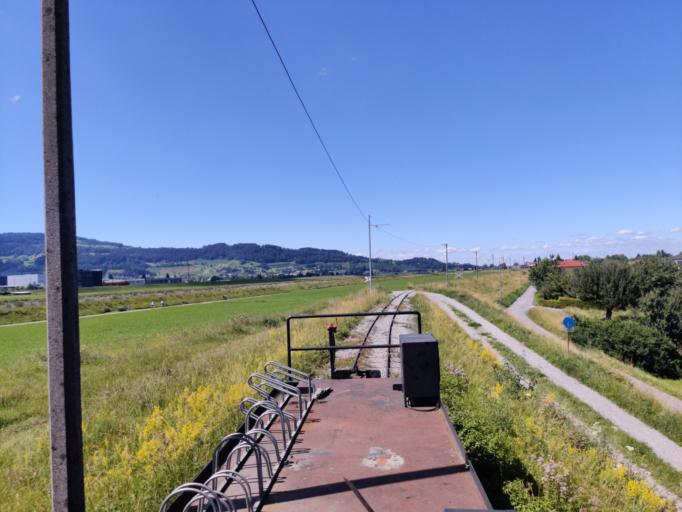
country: AT
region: Vorarlberg
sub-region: Politischer Bezirk Dornbirn
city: Lustenau
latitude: 47.4097
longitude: 9.6536
